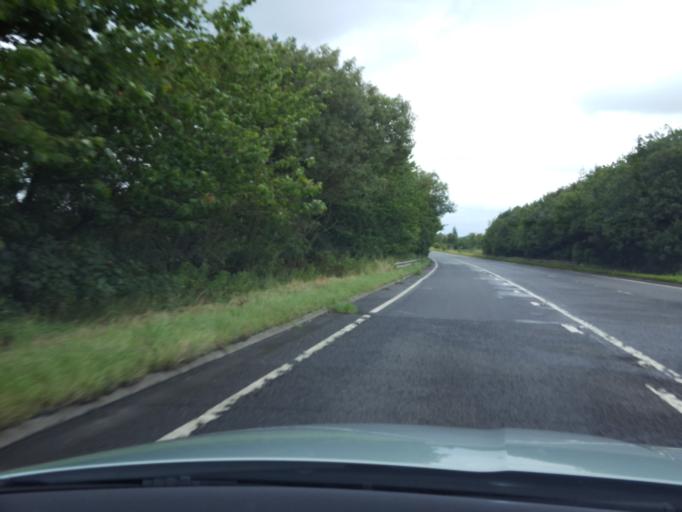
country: GB
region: Scotland
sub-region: West Lothian
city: Bathgate
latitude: 55.9107
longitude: -3.6749
